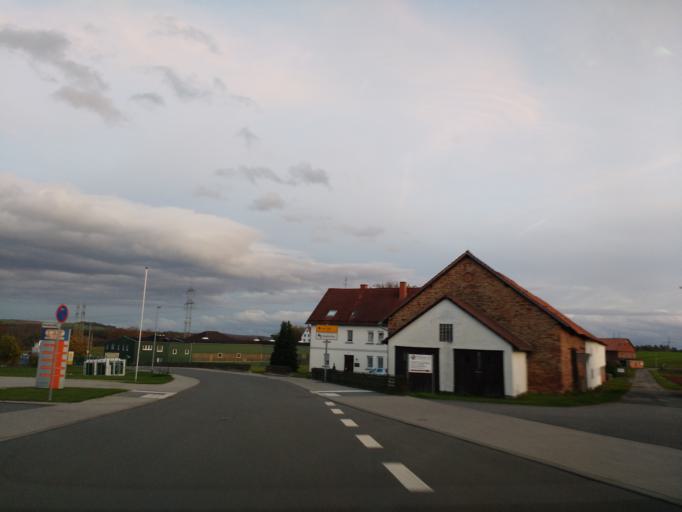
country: DE
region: Hesse
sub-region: Regierungsbezirk Kassel
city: Waldeck
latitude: 51.2038
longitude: 9.0682
